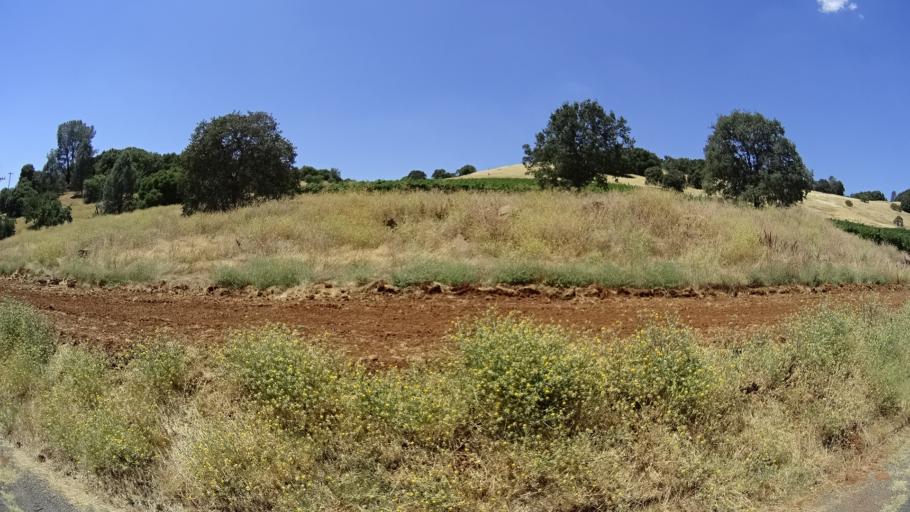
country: US
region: California
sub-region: Calaveras County
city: Angels Camp
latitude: 38.1015
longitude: -120.5023
